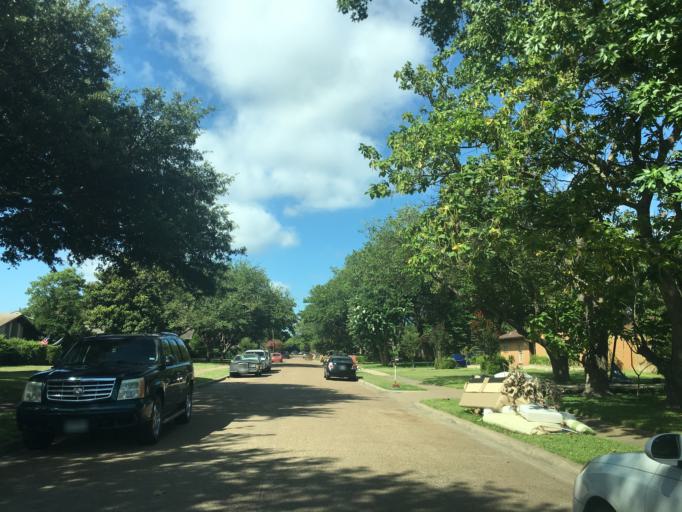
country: US
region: Texas
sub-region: Dallas County
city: Garland
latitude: 32.8481
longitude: -96.6613
